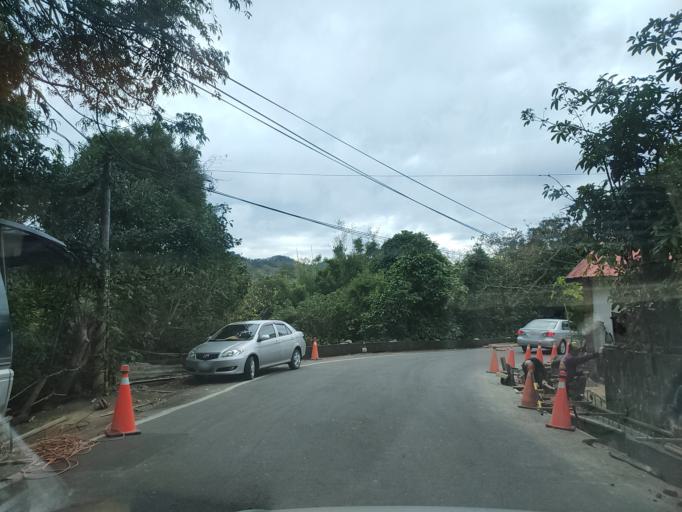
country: TW
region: Taiwan
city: Fengyuan
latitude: 24.3630
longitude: 120.7791
